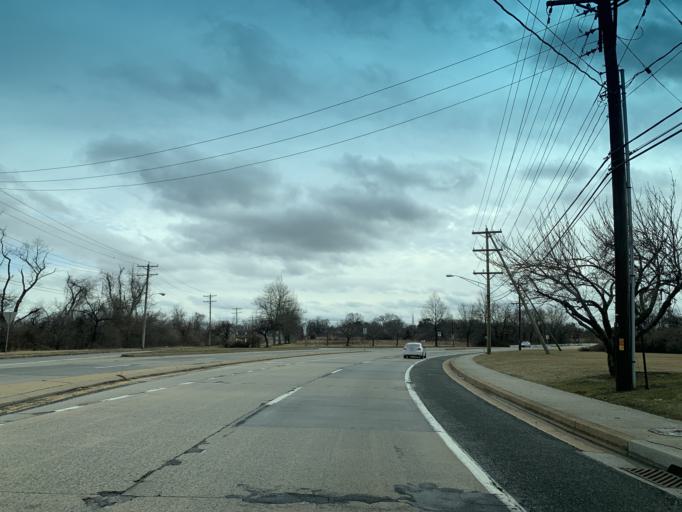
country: US
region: Delaware
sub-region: New Castle County
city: New Castle
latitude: 39.6676
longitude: -75.5607
